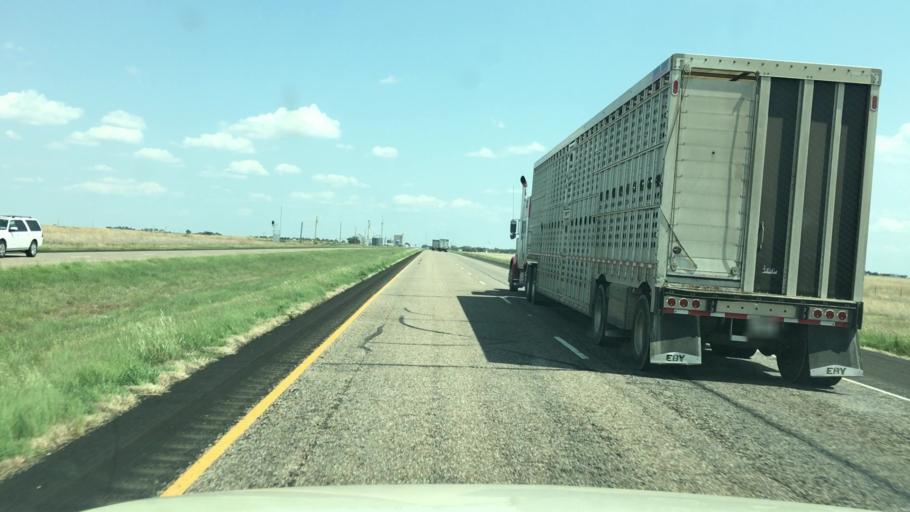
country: US
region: Texas
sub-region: Armstrong County
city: Claude
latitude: 35.1236
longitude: -101.3923
